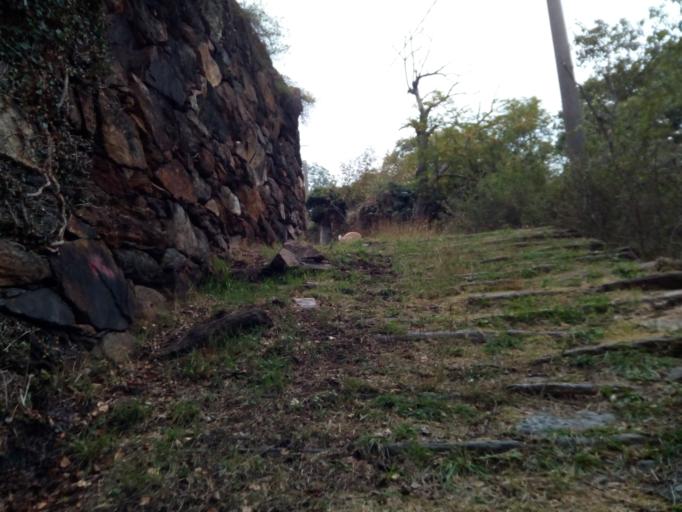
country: IT
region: Piedmont
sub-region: Provincia di Torino
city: Settimo Vittone
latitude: 45.5475
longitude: 7.8392
